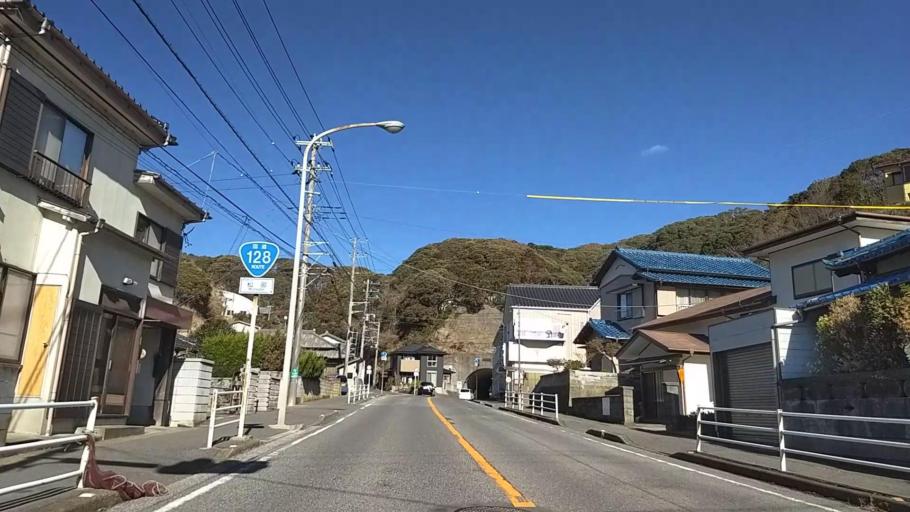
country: JP
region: Chiba
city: Katsuura
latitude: 35.1473
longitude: 140.2937
